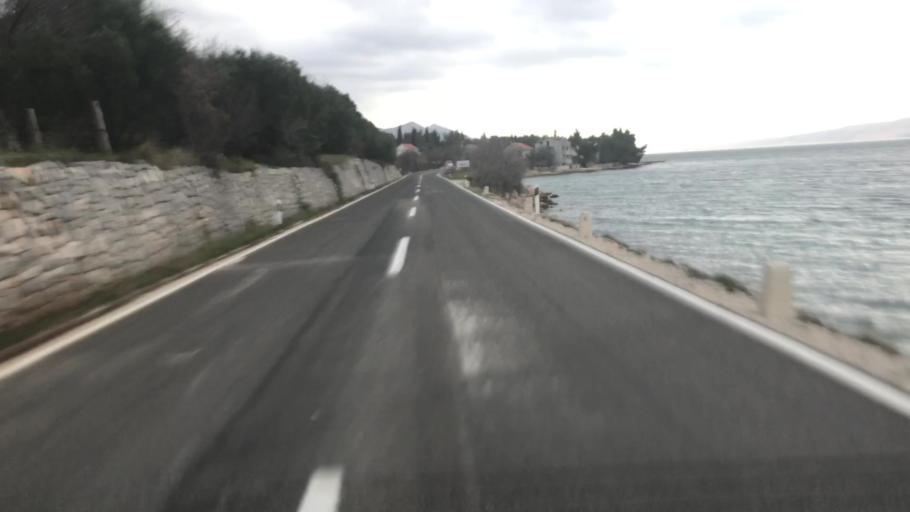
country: HR
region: Zadarska
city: Razanac
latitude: 44.3336
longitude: 15.3561
